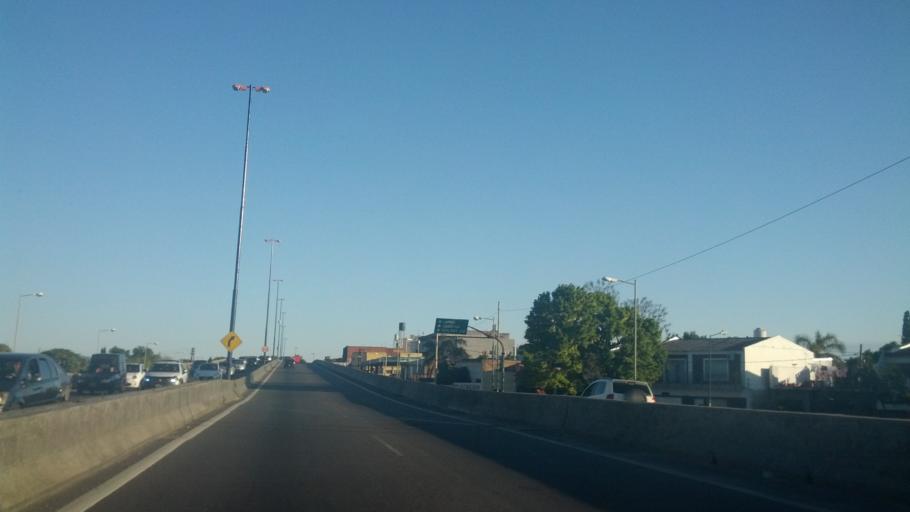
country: AR
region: Buenos Aires
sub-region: Partido de Lomas de Zamora
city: Lomas de Zamora
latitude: -34.7542
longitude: -58.4345
